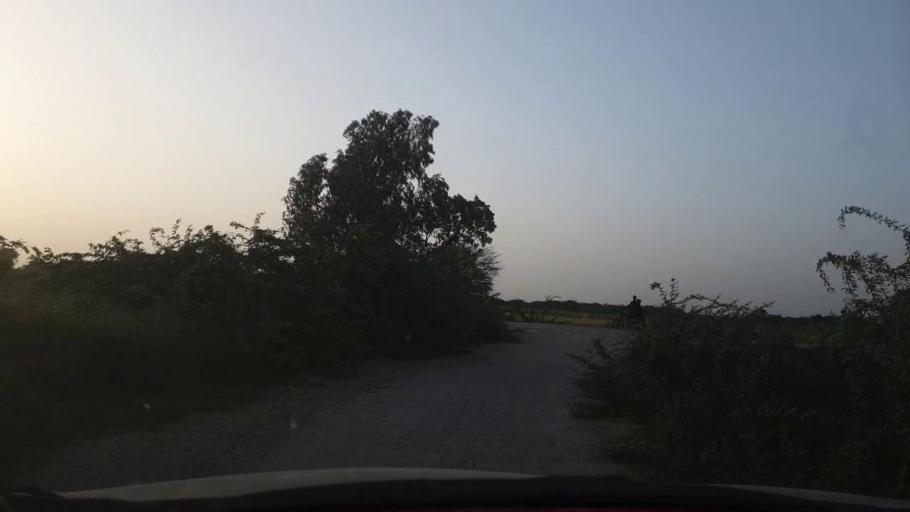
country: PK
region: Sindh
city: Talhar
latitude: 24.9284
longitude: 68.8203
